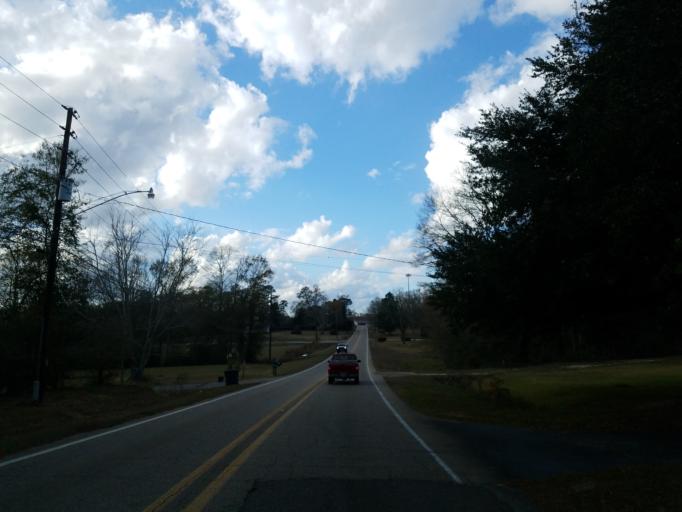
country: US
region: Mississippi
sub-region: Jones County
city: Ellisville
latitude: 31.5944
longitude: -89.1931
